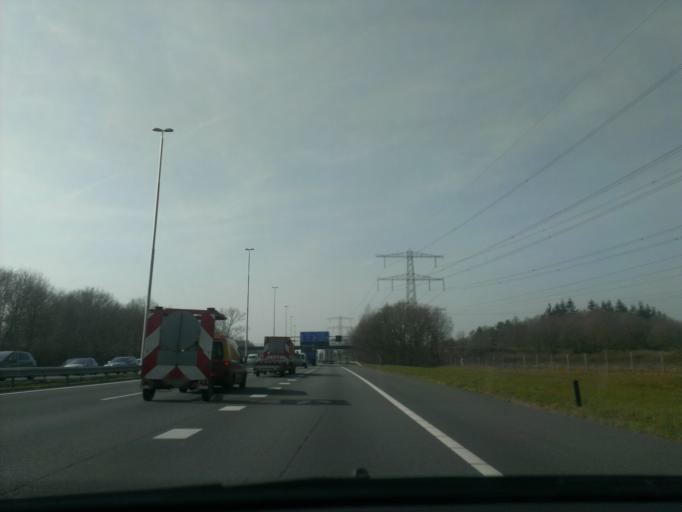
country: NL
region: Overijssel
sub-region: Gemeente Borne
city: Borne
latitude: 52.3033
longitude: 6.7139
